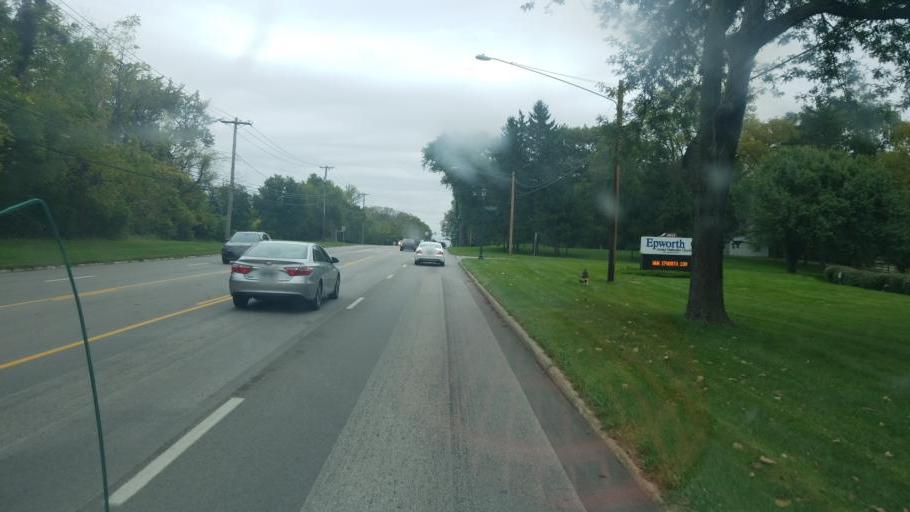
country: US
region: Ohio
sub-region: Lucas County
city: Ottawa Hills
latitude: 41.6769
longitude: -83.6580
